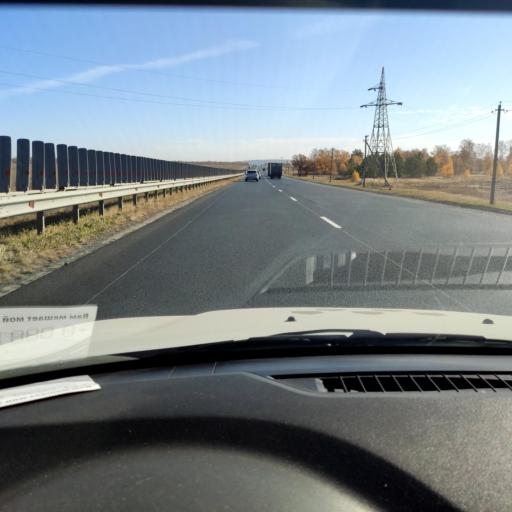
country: RU
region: Samara
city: Bogatyr'
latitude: 53.5105
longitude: 49.9538
